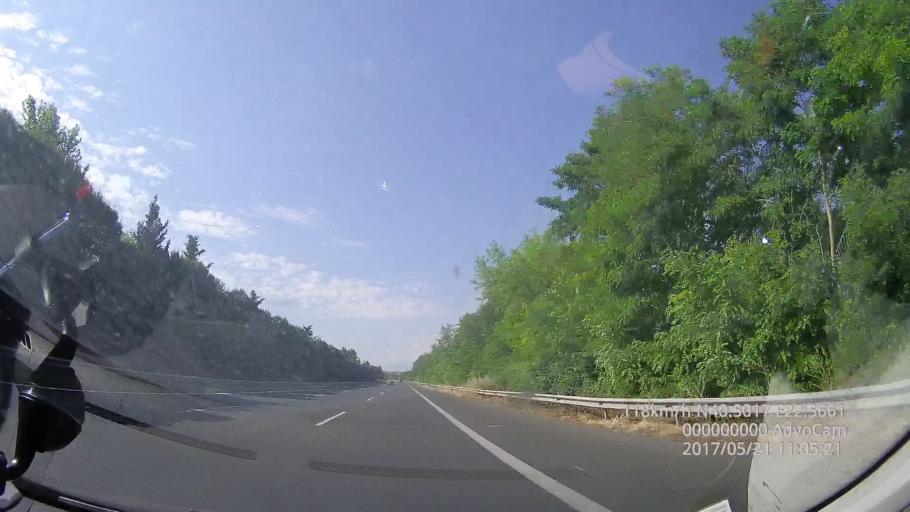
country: GR
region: Central Macedonia
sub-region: Nomos Pierias
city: Aiginio
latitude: 40.5009
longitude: 22.5658
